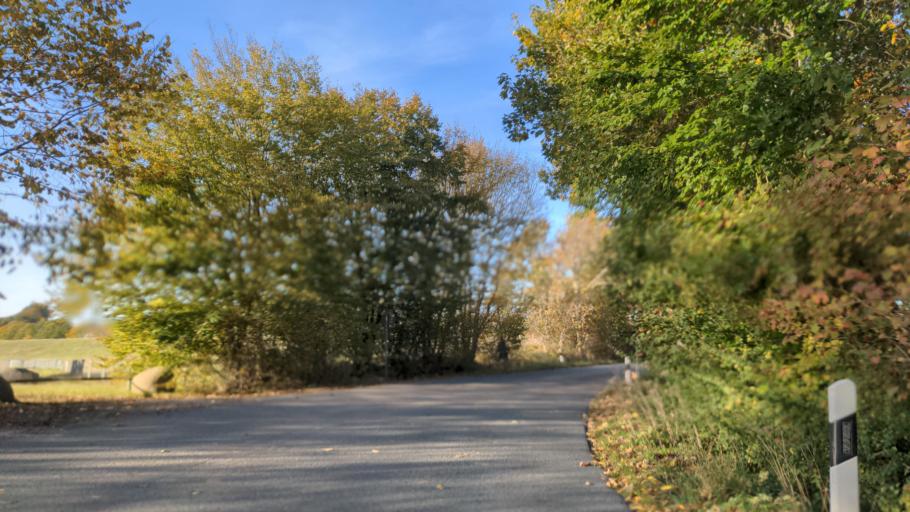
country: DE
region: Schleswig-Holstein
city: Kirchnuchel
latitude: 54.1632
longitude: 10.6689
